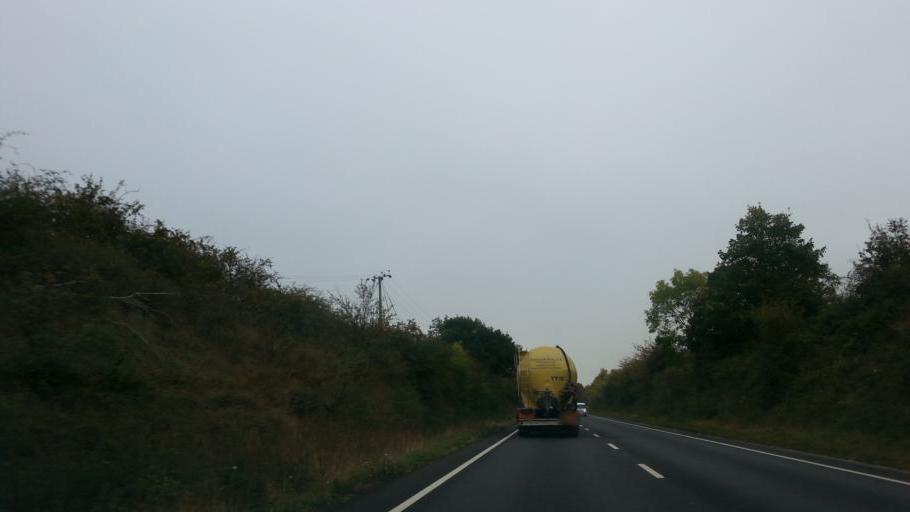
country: GB
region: England
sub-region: Northamptonshire
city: Oundle
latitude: 52.4644
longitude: -0.4606
